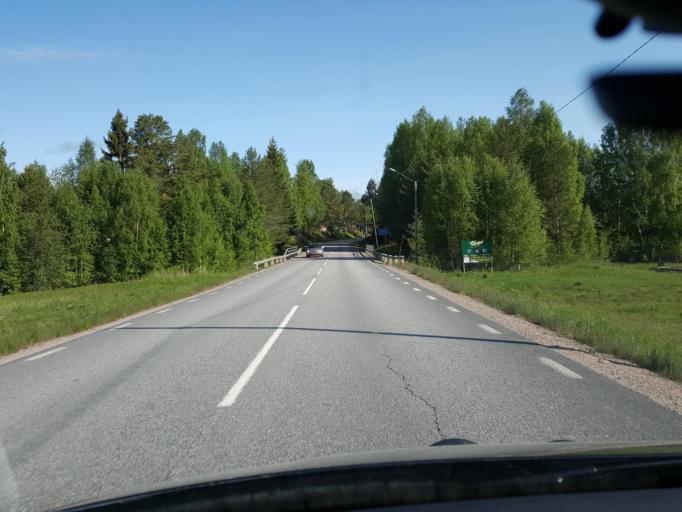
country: SE
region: Vaesternorrland
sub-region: Ange Kommun
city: Ange
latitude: 62.1801
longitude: 15.6534
